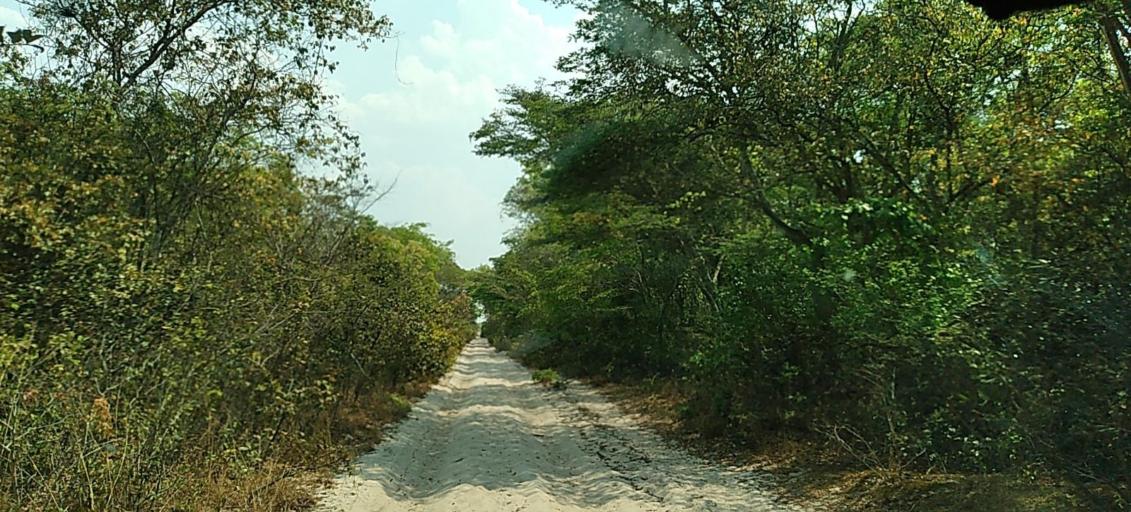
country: ZM
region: North-Western
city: Kabompo
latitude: -13.3888
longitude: 23.7639
